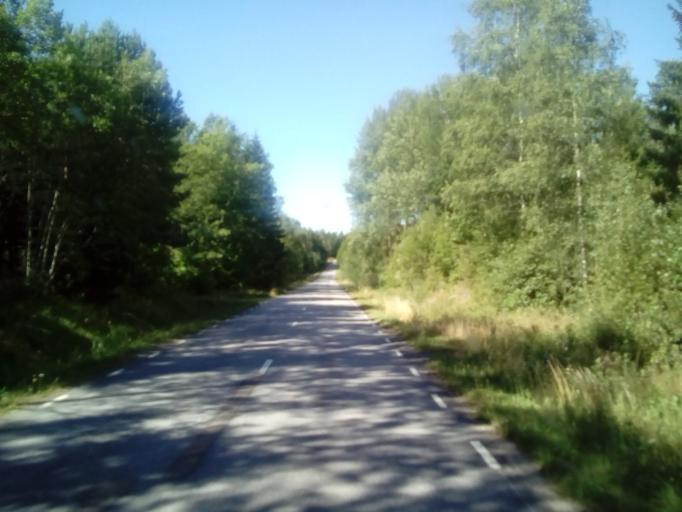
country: SE
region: Kalmar
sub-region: Vimmerby Kommun
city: Sodra Vi
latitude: 57.9051
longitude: 16.0306
